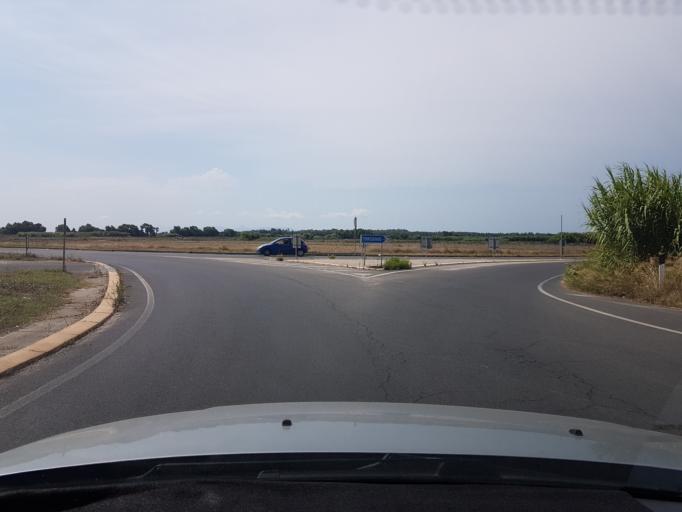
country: IT
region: Sardinia
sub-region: Provincia di Oristano
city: Cabras
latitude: 39.9143
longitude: 8.5419
